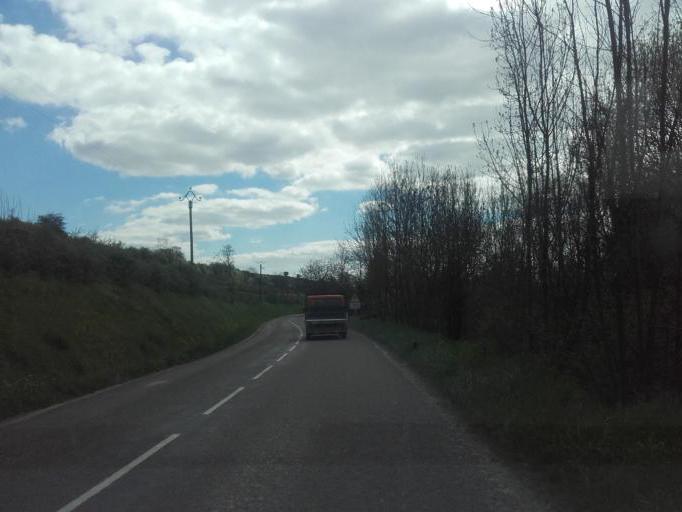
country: FR
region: Bourgogne
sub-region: Departement de la Cote-d'Or
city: Meursault
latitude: 47.0170
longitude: 4.7829
